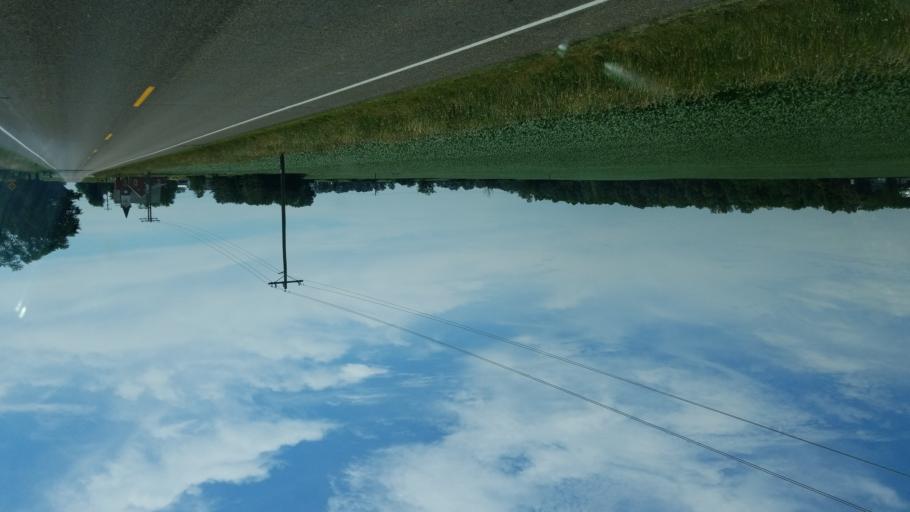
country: US
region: Michigan
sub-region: Eaton County
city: Charlotte
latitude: 42.6260
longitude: -84.8209
